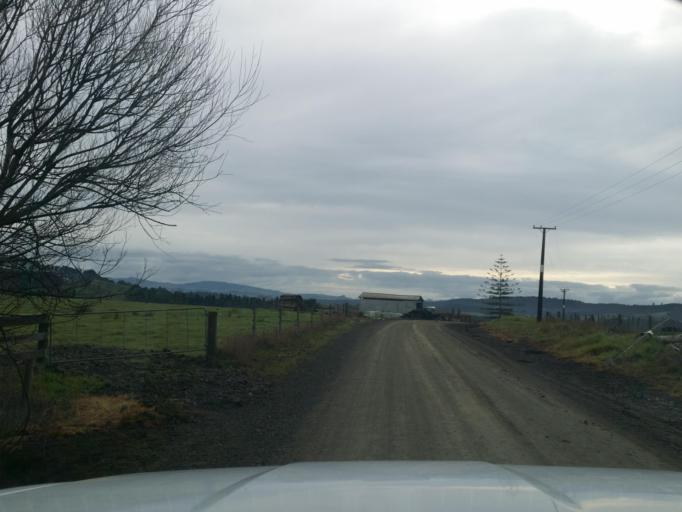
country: NZ
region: Northland
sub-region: Whangarei
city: Maungatapere
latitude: -35.8033
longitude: 174.0494
